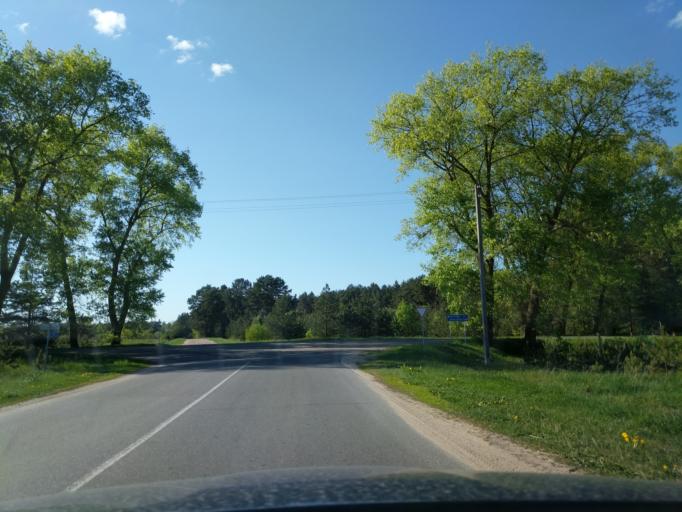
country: BY
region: Vitebsk
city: Pastavy
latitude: 55.1593
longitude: 26.9846
